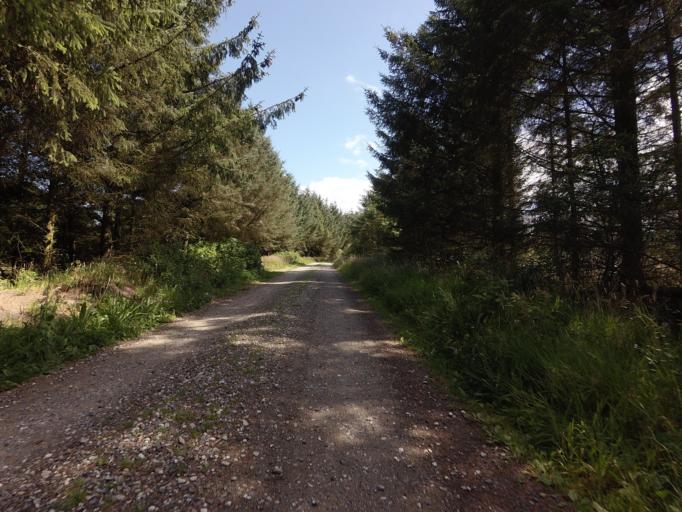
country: DK
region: North Denmark
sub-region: Jammerbugt Kommune
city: Pandrup
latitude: 57.3020
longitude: 9.6566
